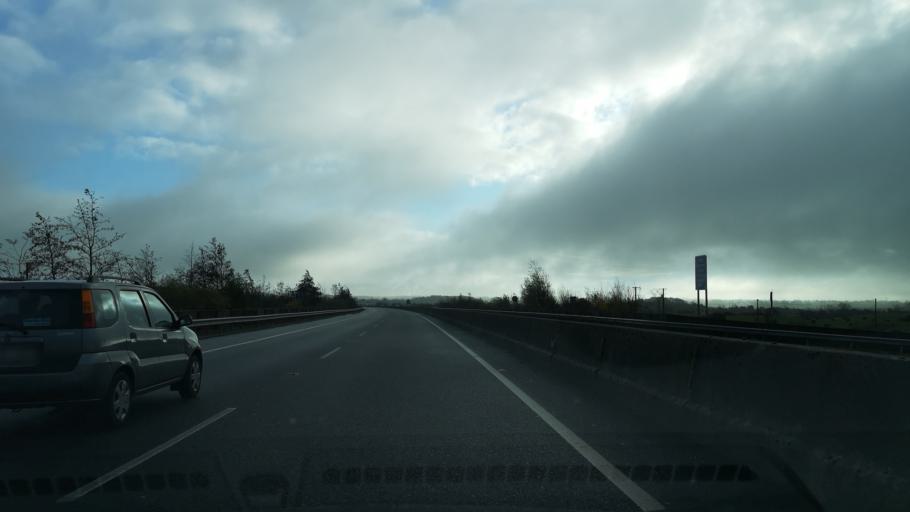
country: IE
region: Connaught
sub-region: County Galway
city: Athenry
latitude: 53.2710
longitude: -8.6732
